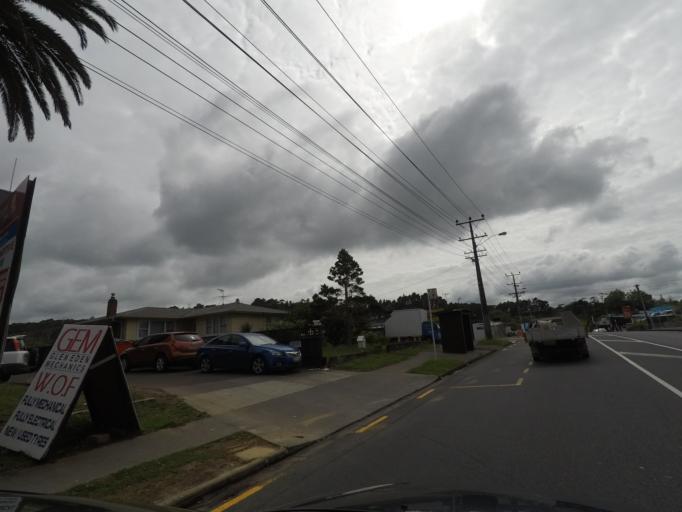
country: NZ
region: Auckland
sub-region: Auckland
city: Waitakere
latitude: -36.9088
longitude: 174.6397
